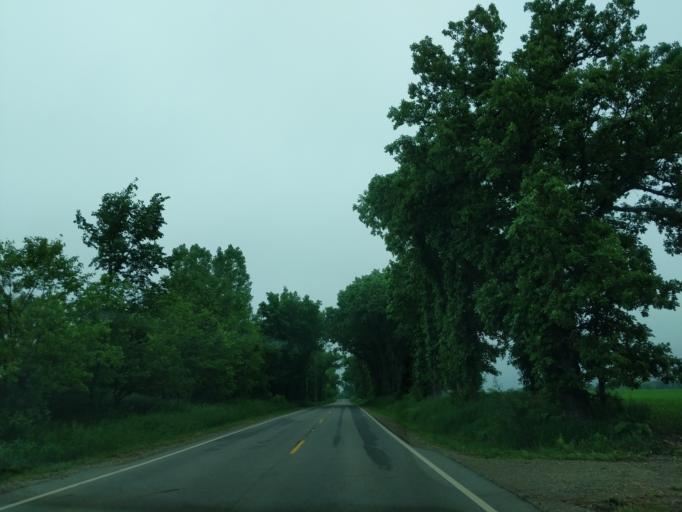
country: US
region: Michigan
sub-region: Jackson County
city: Spring Arbor
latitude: 42.2105
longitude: -84.5702
